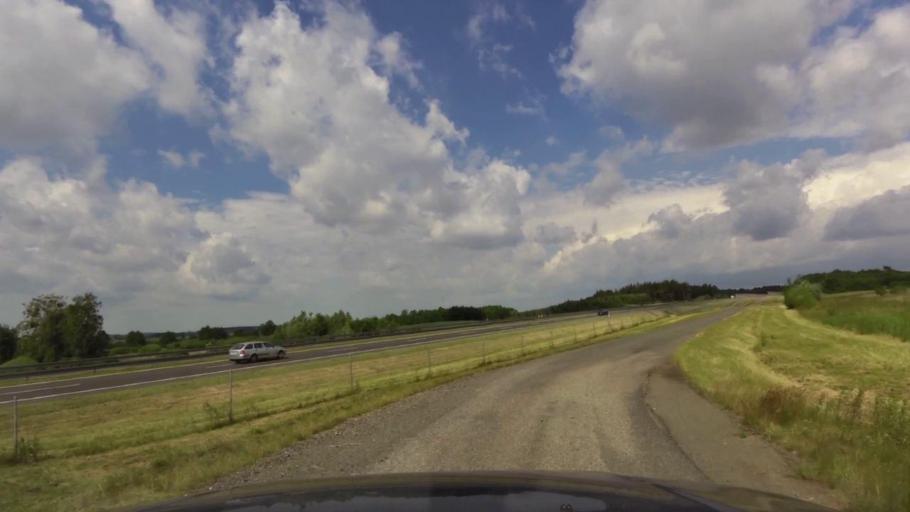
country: PL
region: West Pomeranian Voivodeship
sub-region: Powiat pyrzycki
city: Lipiany
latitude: 52.9596
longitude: 14.9293
